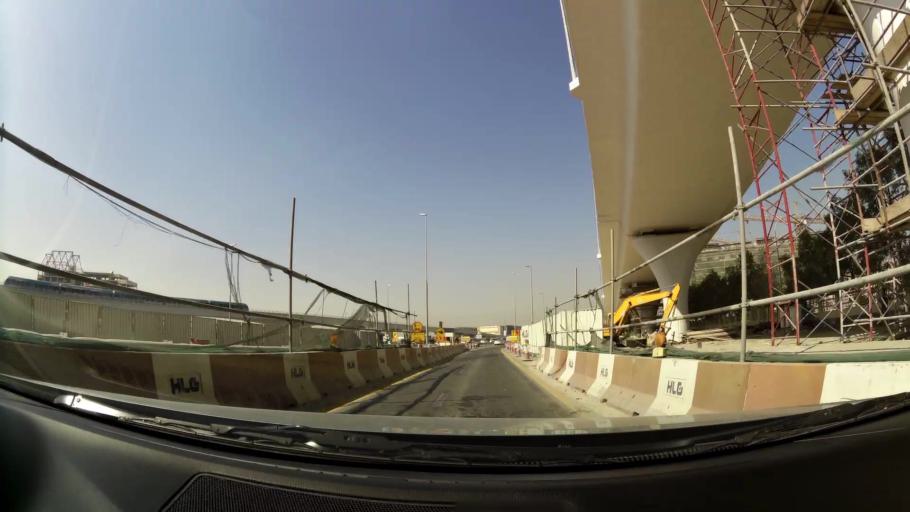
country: AE
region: Dubai
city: Dubai
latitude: 25.0640
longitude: 55.1313
